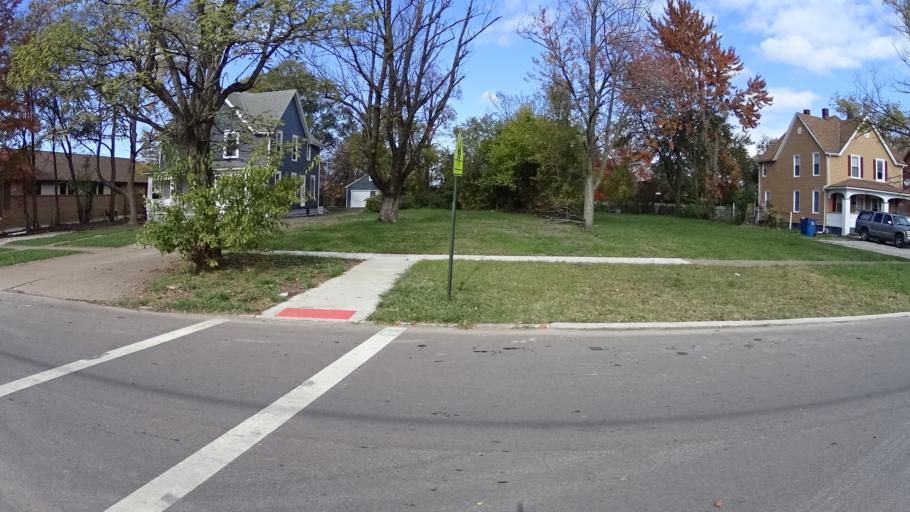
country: US
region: Ohio
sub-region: Lorain County
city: Lorain
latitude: 41.4421
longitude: -82.1446
